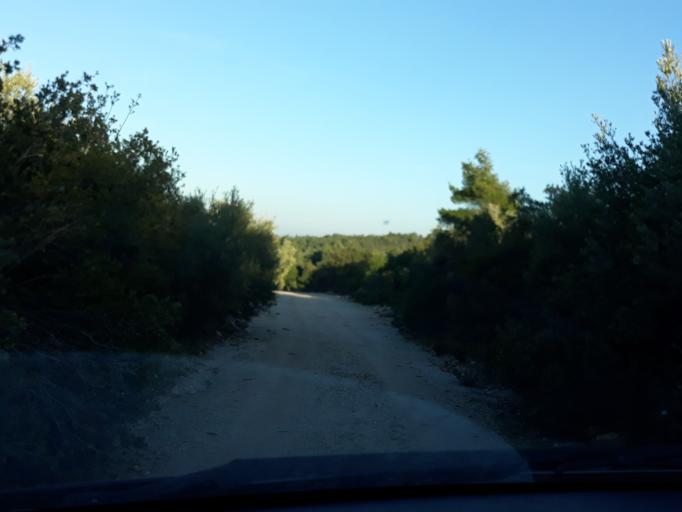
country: GR
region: Central Greece
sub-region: Nomos Voiotias
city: Asopia
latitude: 38.2704
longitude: 23.5297
